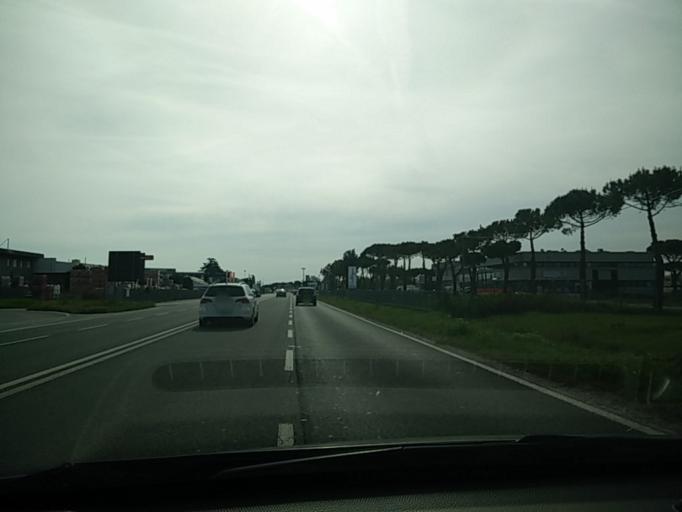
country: IT
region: Emilia-Romagna
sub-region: Provincia di Rimini
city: Rimini
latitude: 44.0663
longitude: 12.5287
